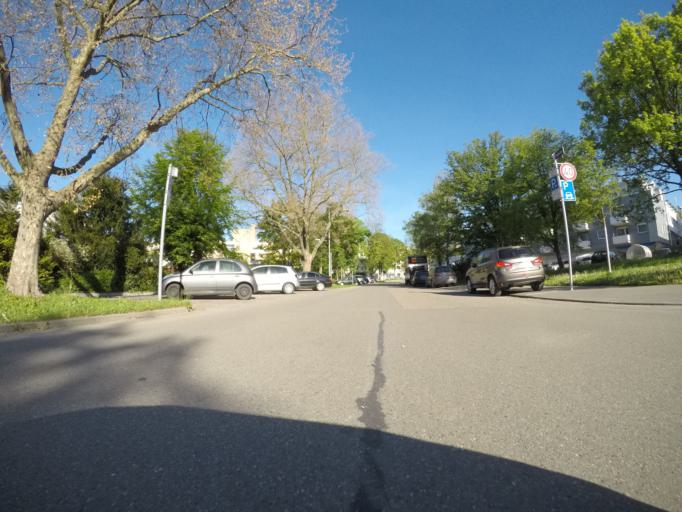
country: DE
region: Baden-Wuerttemberg
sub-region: Regierungsbezirk Stuttgart
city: Gerlingen
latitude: 48.8043
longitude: 9.0908
